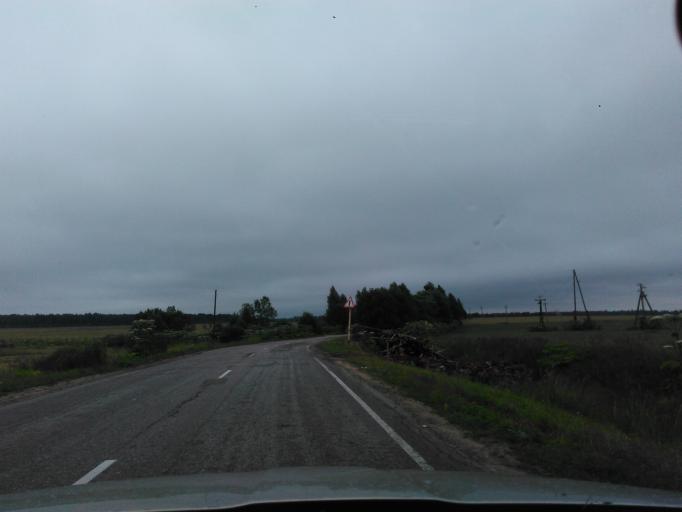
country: RU
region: Tverskaya
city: Zavidovo
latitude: 56.6103
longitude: 36.6360
